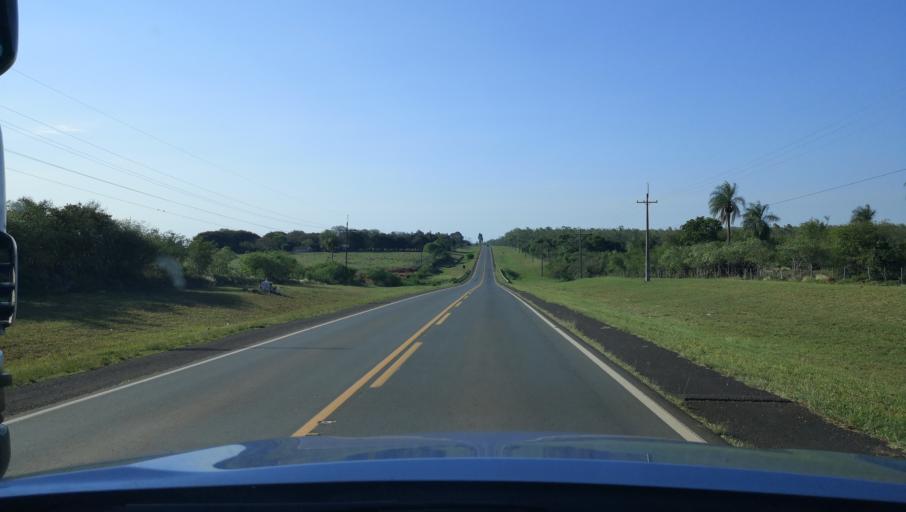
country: PY
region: Misiones
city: Santa Maria
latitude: -26.7716
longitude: -57.0304
